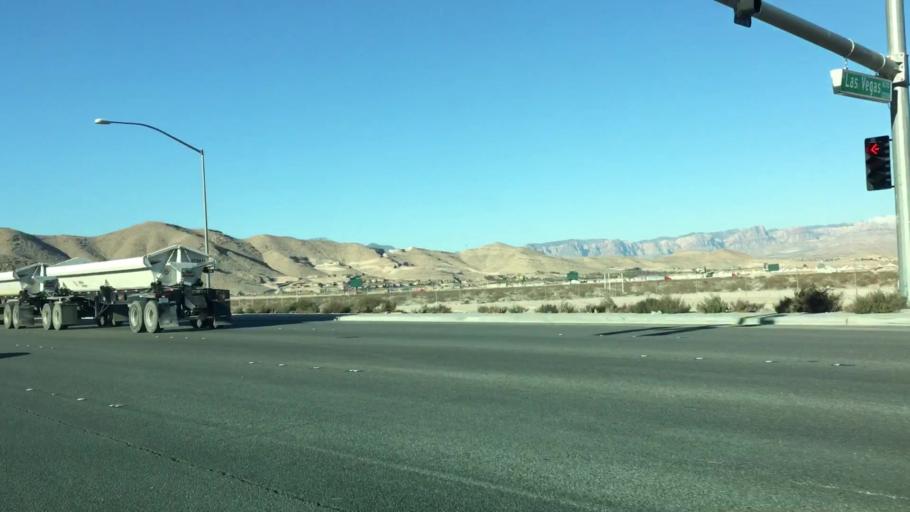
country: US
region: Nevada
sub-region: Clark County
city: Enterprise
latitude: 35.9653
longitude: -115.1730
